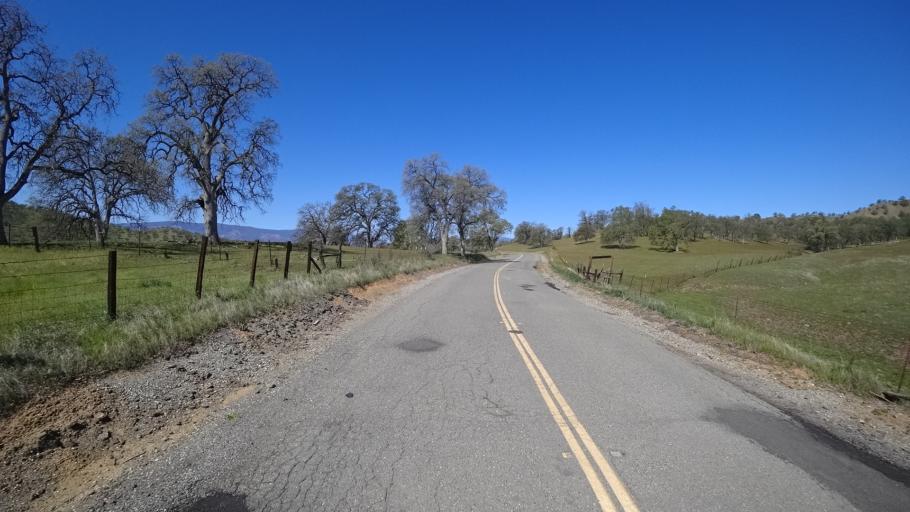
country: US
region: California
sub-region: Tehama County
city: Rancho Tehama Reserve
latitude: 39.7864
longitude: -122.4813
